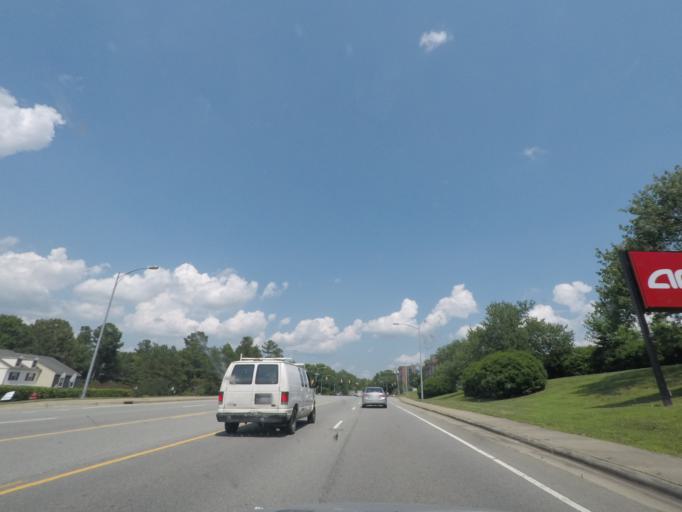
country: US
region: North Carolina
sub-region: Durham County
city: Durham
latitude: 35.9608
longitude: -78.9573
